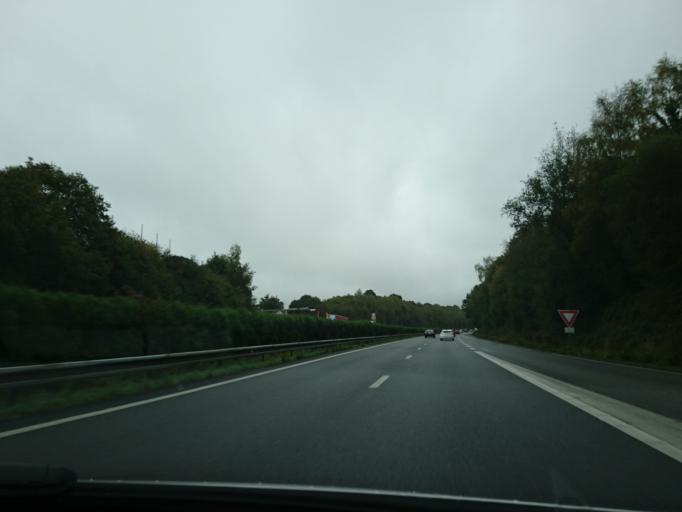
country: FR
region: Brittany
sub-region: Departement du Finistere
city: Redene
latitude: 47.8210
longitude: -3.4674
